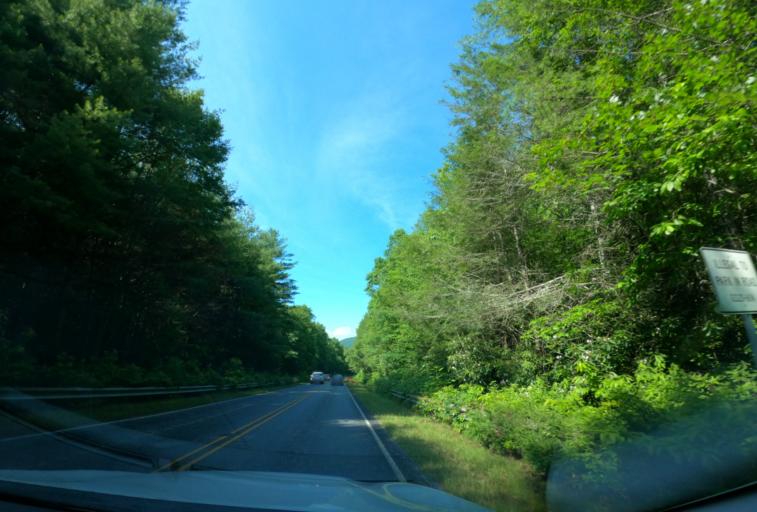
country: US
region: North Carolina
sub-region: Transylvania County
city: Brevard
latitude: 35.1962
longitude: -82.6234
